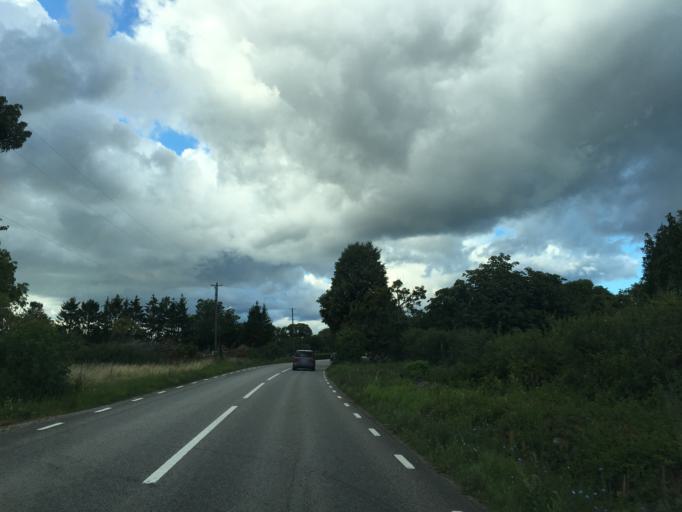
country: SE
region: Kalmar
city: Faerjestaden
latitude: 56.6411
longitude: 16.5164
